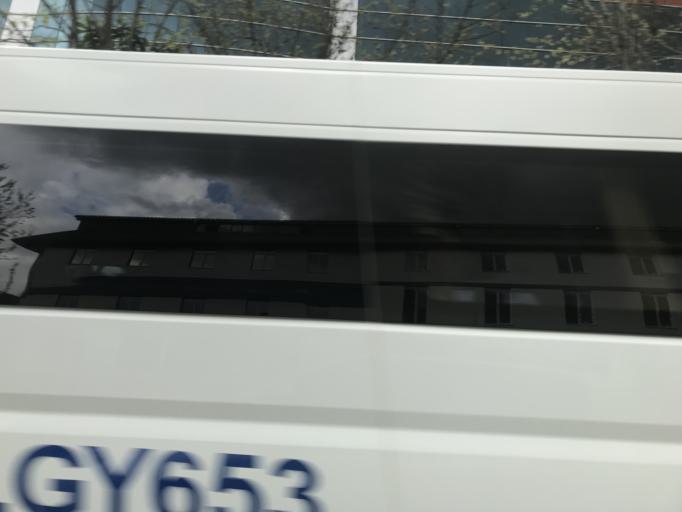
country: TR
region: Istanbul
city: Samandira
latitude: 40.9966
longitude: 29.1781
